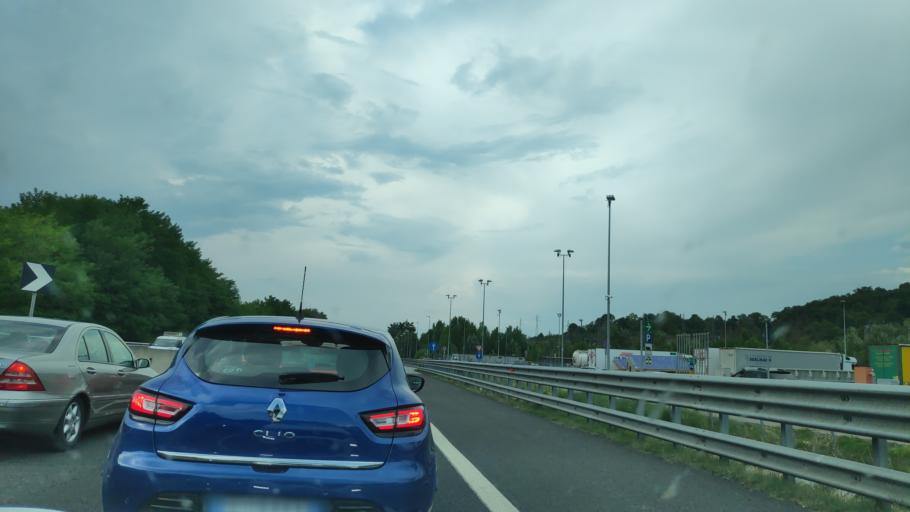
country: IT
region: Tuscany
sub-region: Province of Arezzo
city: San Giovanni Valdarno
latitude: 43.5833
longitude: 11.5212
